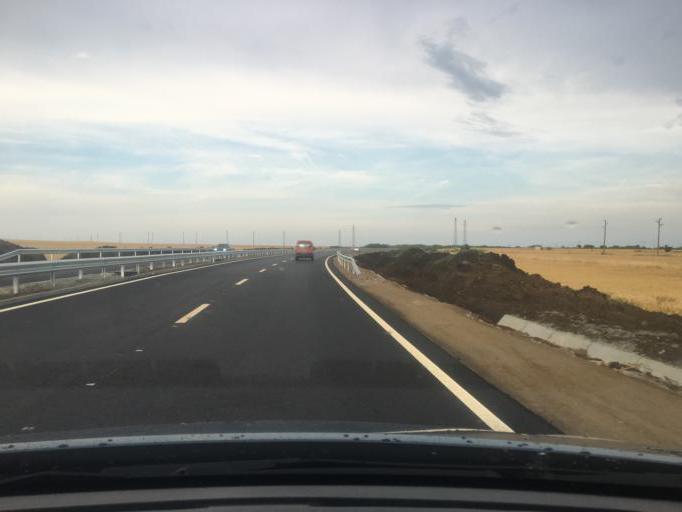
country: BG
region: Burgas
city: Aheloy
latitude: 42.6563
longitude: 27.6548
